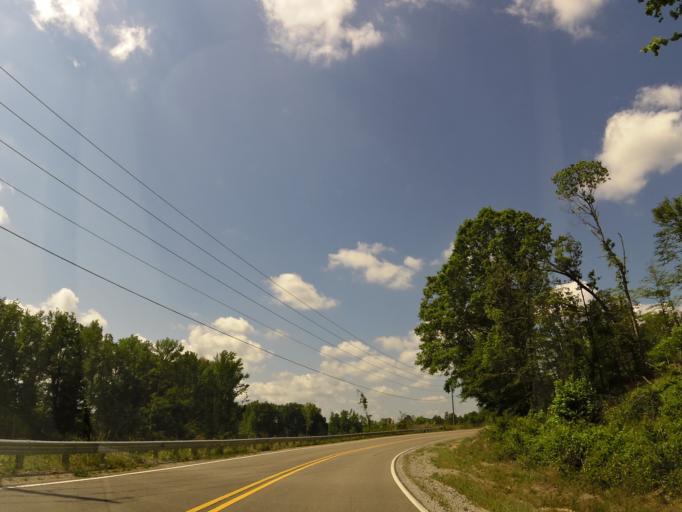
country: US
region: Alabama
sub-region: Marion County
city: Guin
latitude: 33.9972
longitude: -87.8626
